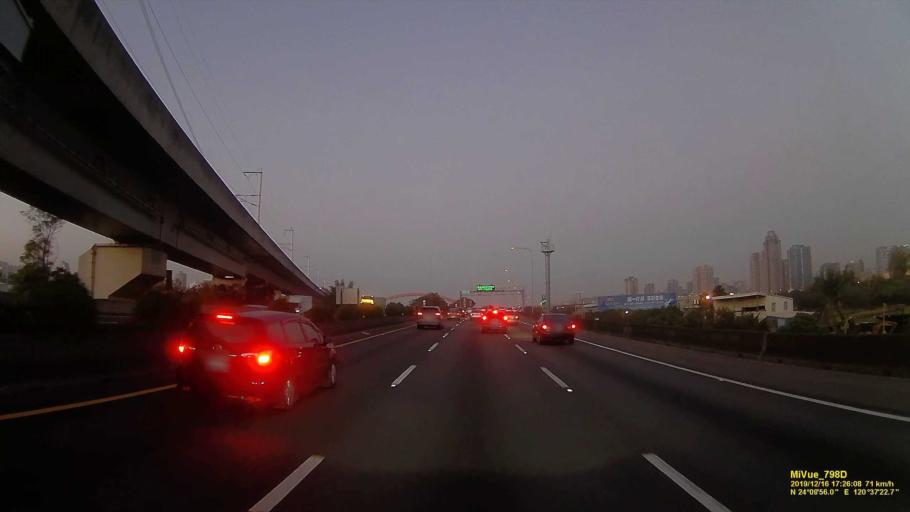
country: TW
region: Taiwan
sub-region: Taichung City
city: Taichung
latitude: 24.1659
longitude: 120.6232
